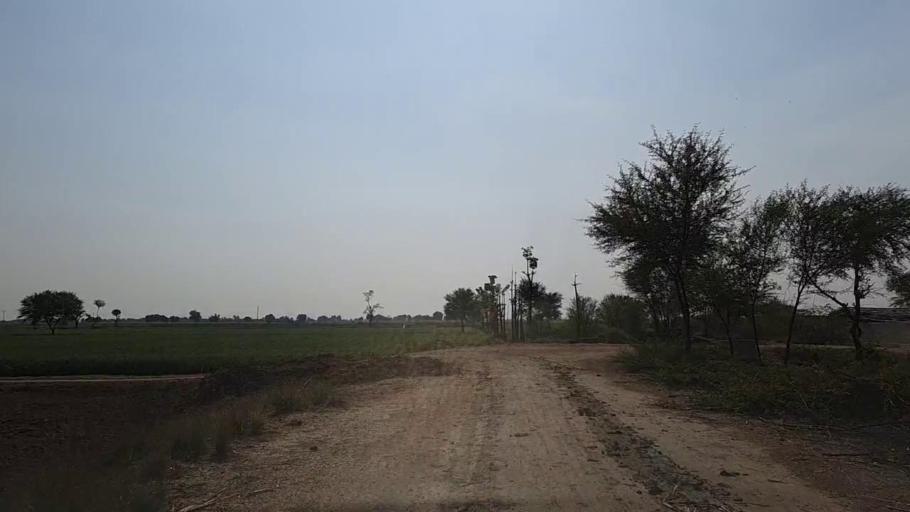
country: PK
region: Sindh
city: Nawabshah
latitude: 26.2870
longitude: 68.4804
